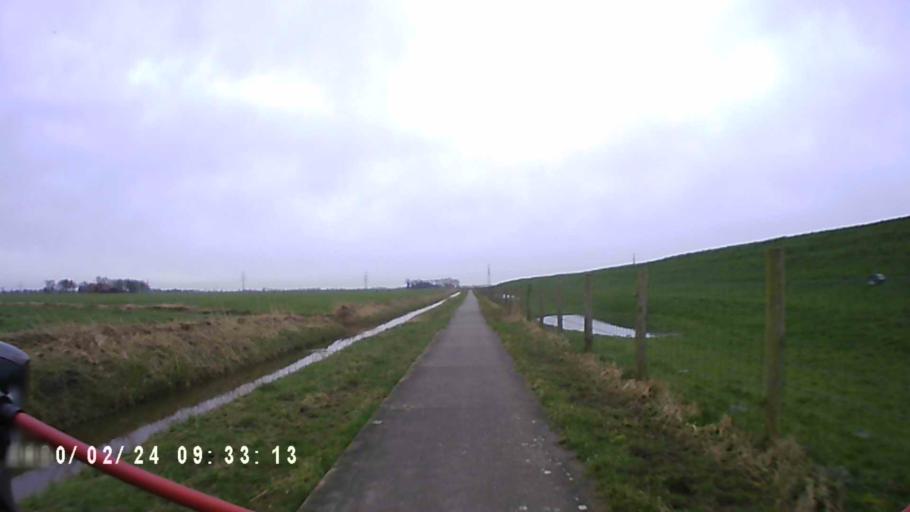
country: NL
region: Groningen
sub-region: Gemeente Winsum
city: Winsum
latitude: 53.3021
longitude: 6.4991
